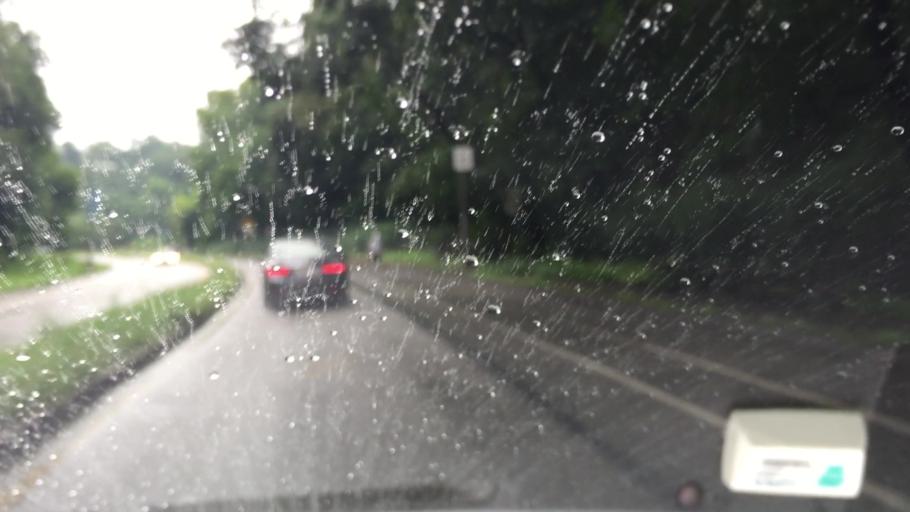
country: US
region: Pennsylvania
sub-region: Allegheny County
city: Aspinwall
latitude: 40.4687
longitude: -79.9115
